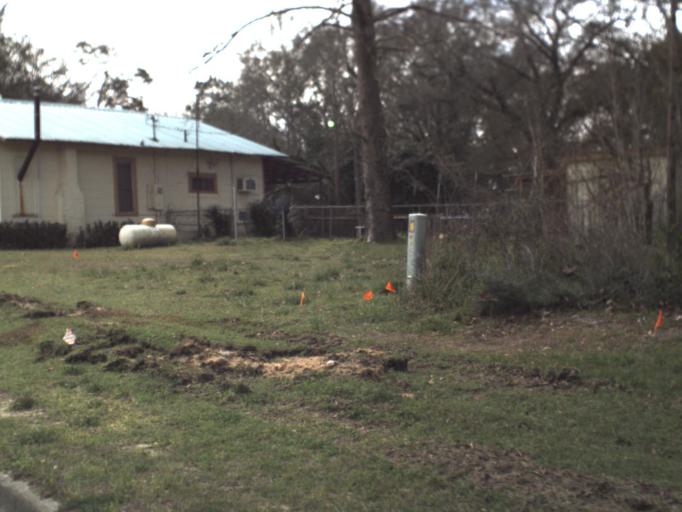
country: US
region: Florida
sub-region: Washington County
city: Chipley
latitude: 30.6525
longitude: -85.3952
